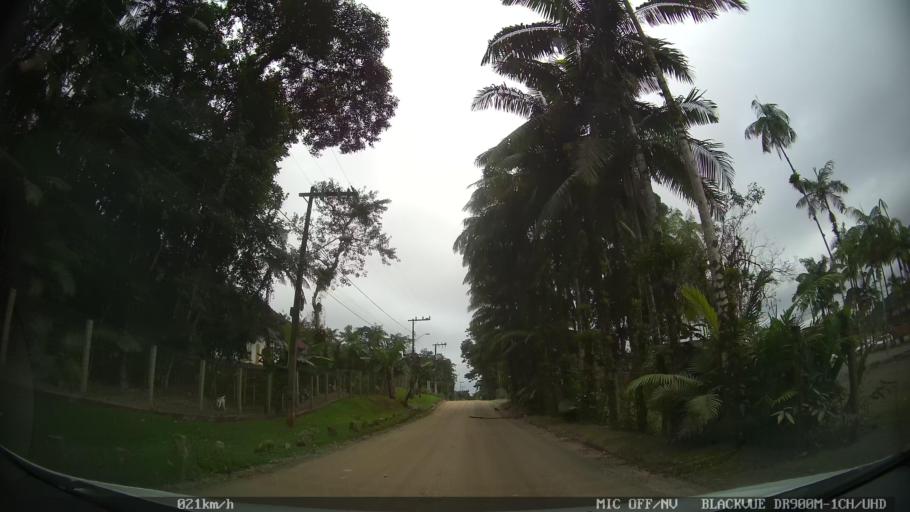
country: BR
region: Santa Catarina
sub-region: Joinville
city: Joinville
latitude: -26.2764
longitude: -48.9372
